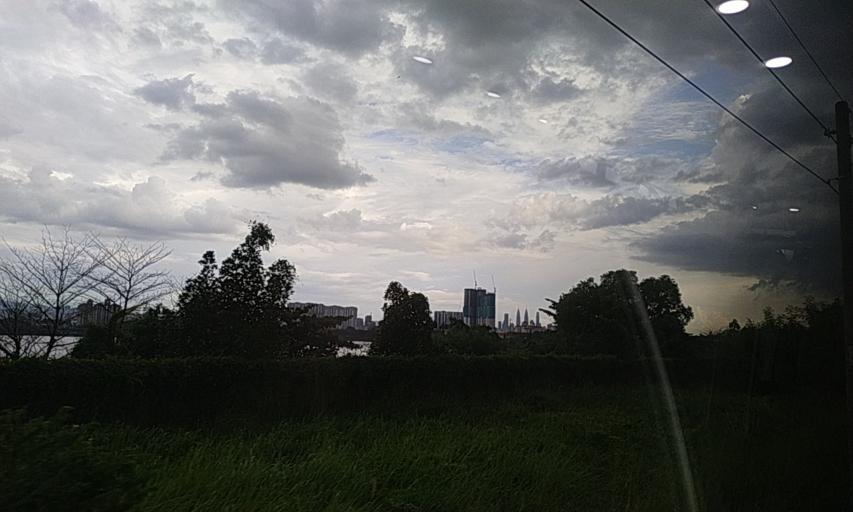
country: MY
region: Kuala Lumpur
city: Kuala Lumpur
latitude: 3.2241
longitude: 101.6727
